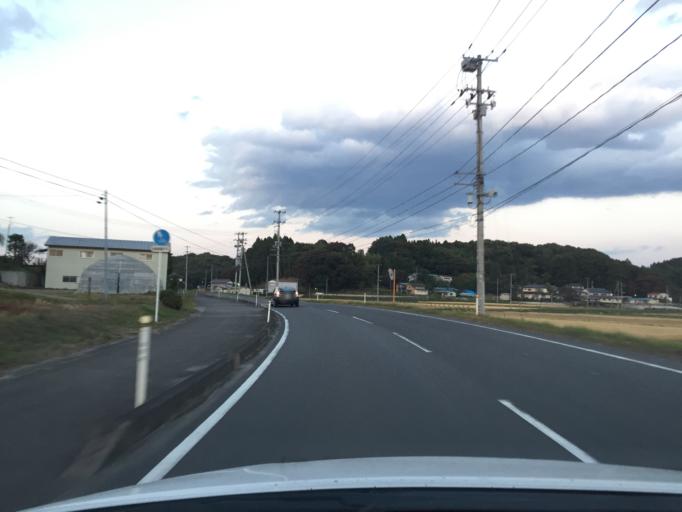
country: JP
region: Fukushima
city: Motomiya
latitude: 37.4995
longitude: 140.4556
